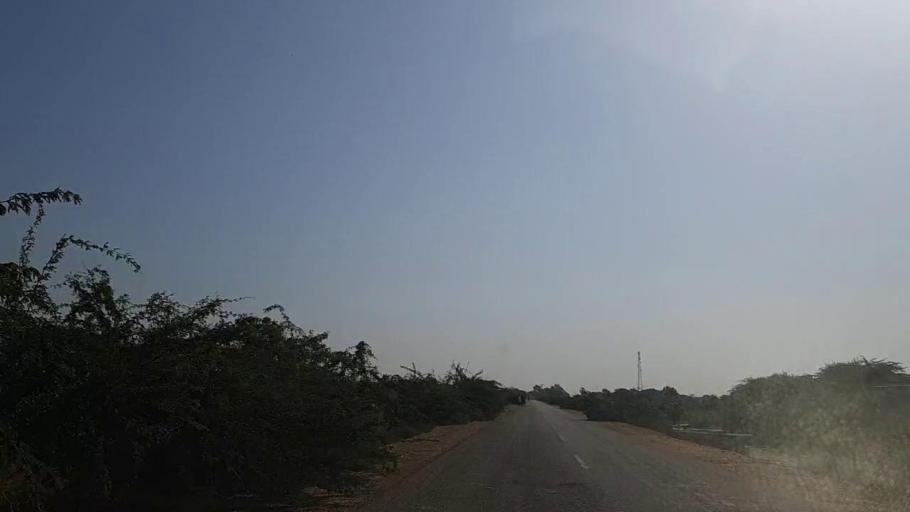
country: PK
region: Sindh
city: Jati
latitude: 24.5219
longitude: 68.2764
